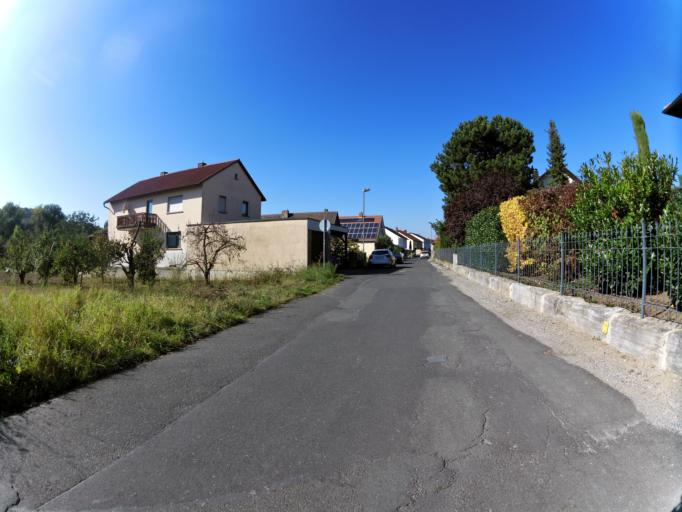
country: DE
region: Bavaria
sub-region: Regierungsbezirk Unterfranken
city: Ochsenfurt
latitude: 49.6702
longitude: 10.0547
